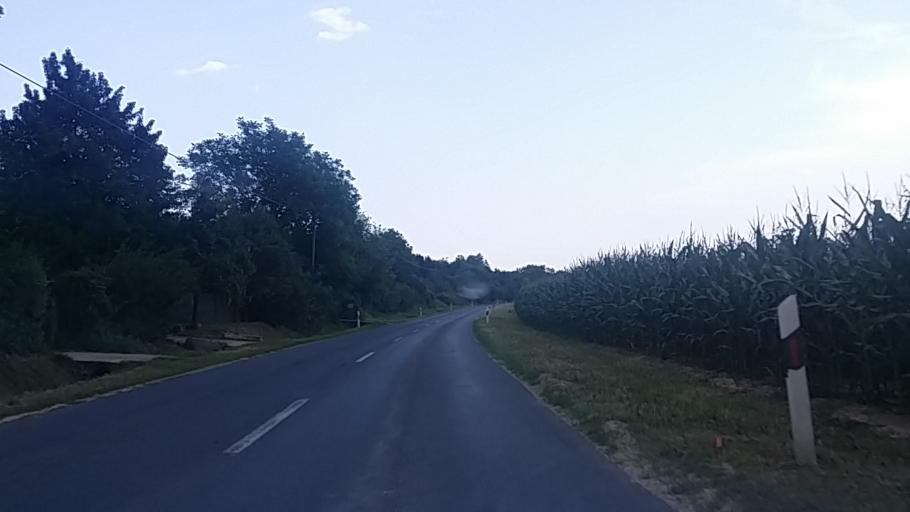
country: HU
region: Zala
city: Cserszegtomaj
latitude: 46.8257
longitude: 17.2003
